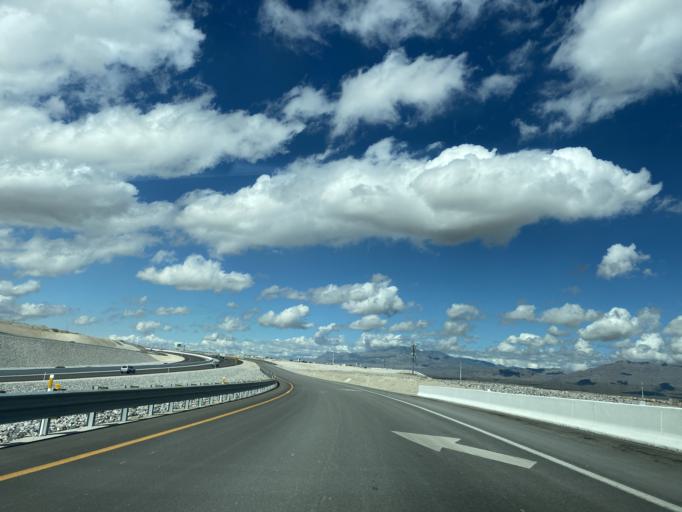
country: US
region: Nevada
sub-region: Clark County
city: Summerlin South
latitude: 36.2491
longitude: -115.3165
